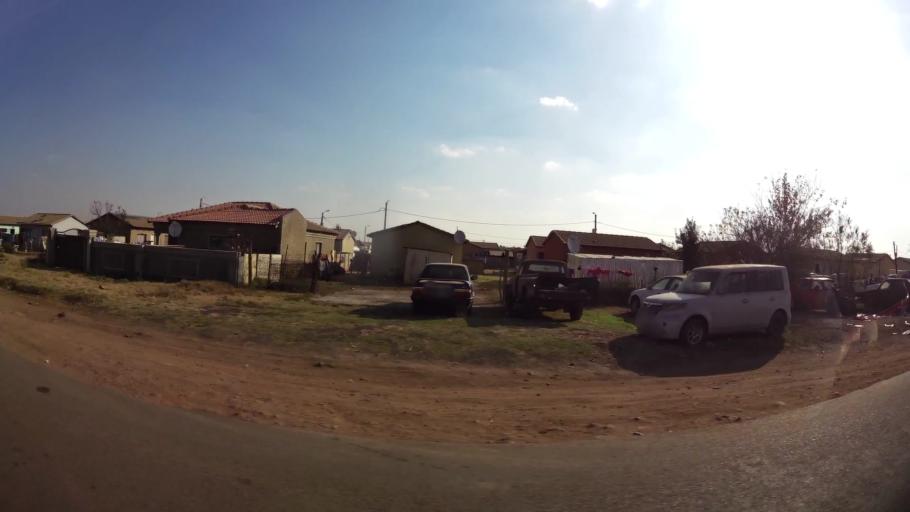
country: ZA
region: Gauteng
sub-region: Ekurhuleni Metropolitan Municipality
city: Benoni
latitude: -26.1555
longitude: 28.3970
